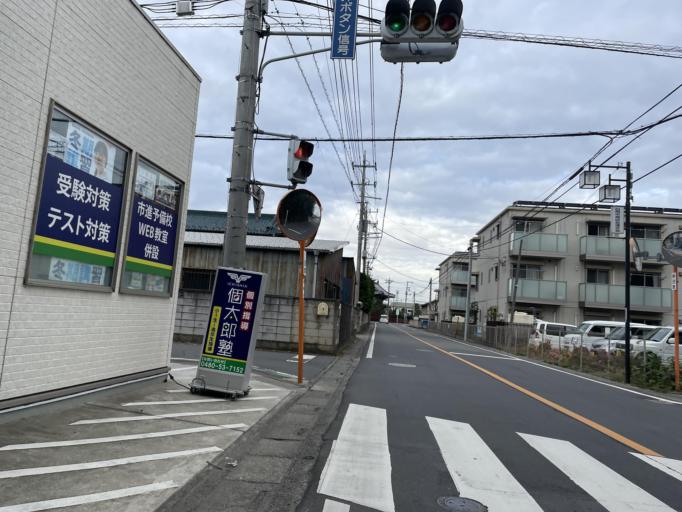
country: JP
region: Saitama
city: Shiraoka
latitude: 36.0210
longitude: 139.6600
